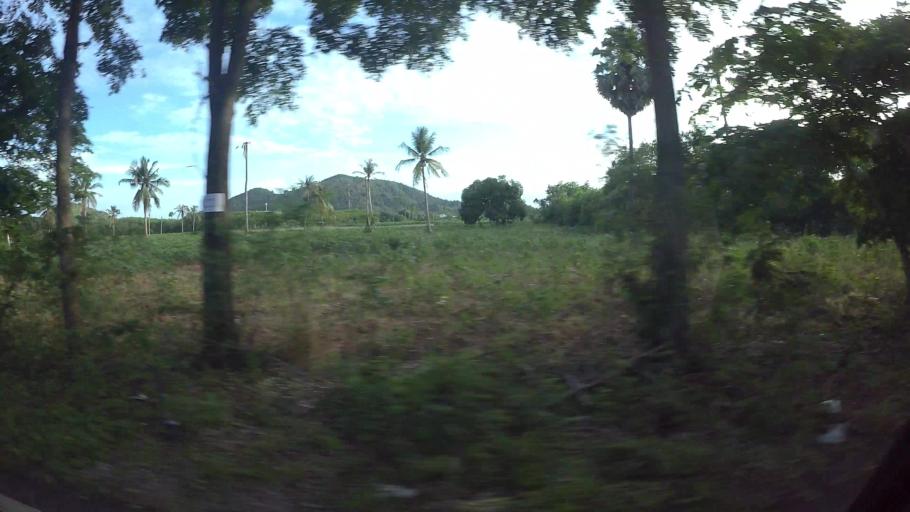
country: TH
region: Chon Buri
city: Sattahip
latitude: 12.7395
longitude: 100.9372
